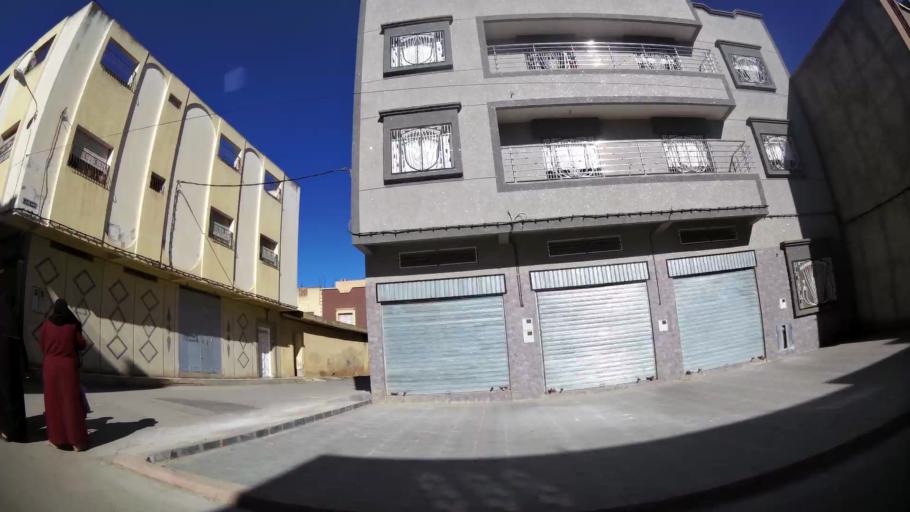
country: MA
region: Oriental
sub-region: Berkane-Taourirt
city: Ahfir
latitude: 34.9570
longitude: -2.1018
